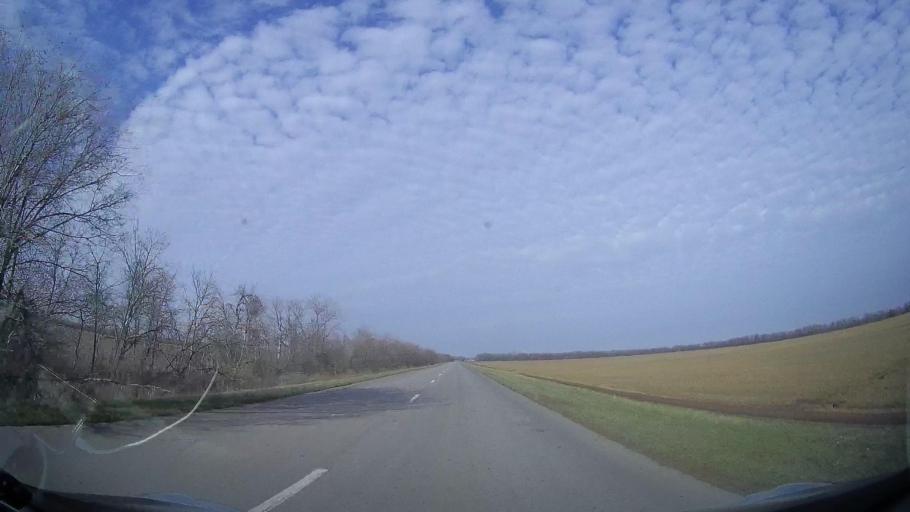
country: RU
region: Rostov
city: Gigant
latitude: 46.8243
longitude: 41.3394
